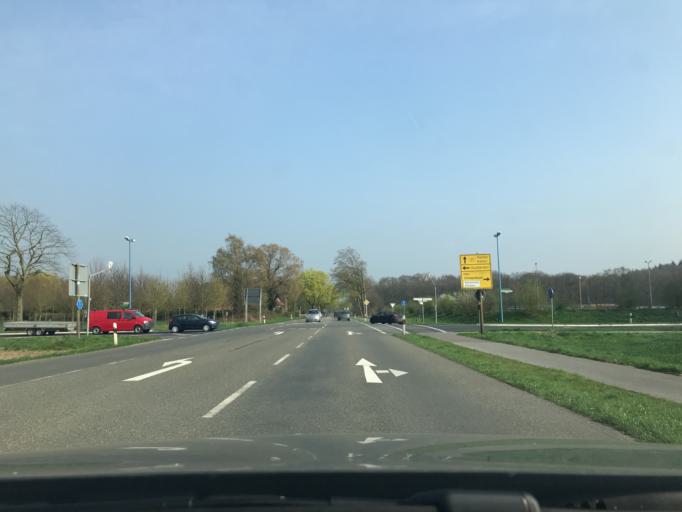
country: DE
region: North Rhine-Westphalia
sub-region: Regierungsbezirk Dusseldorf
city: Kleve
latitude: 51.7653
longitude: 6.2064
